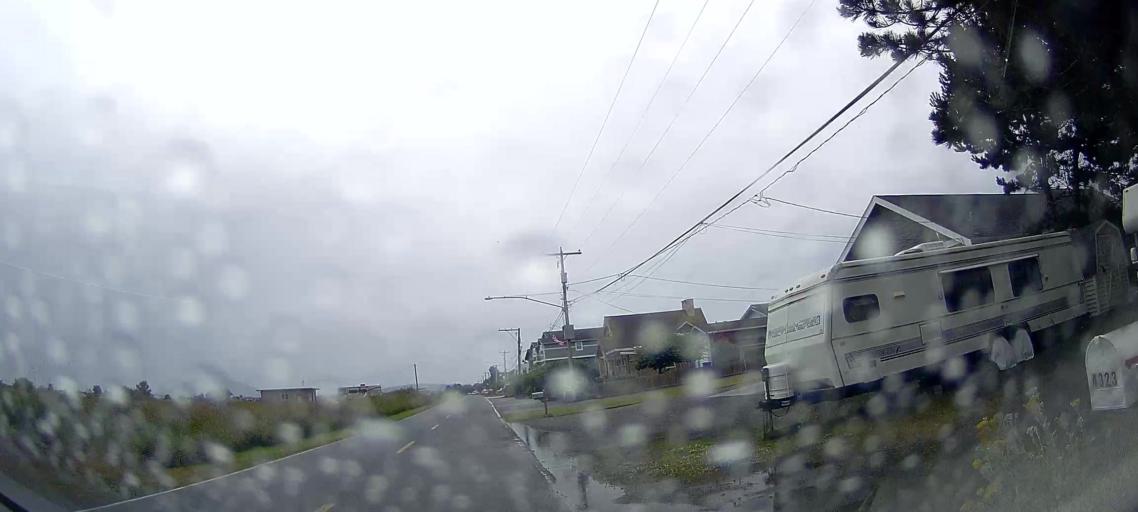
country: US
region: Washington
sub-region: Whatcom County
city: Birch Bay
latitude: 48.7987
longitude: -122.7100
